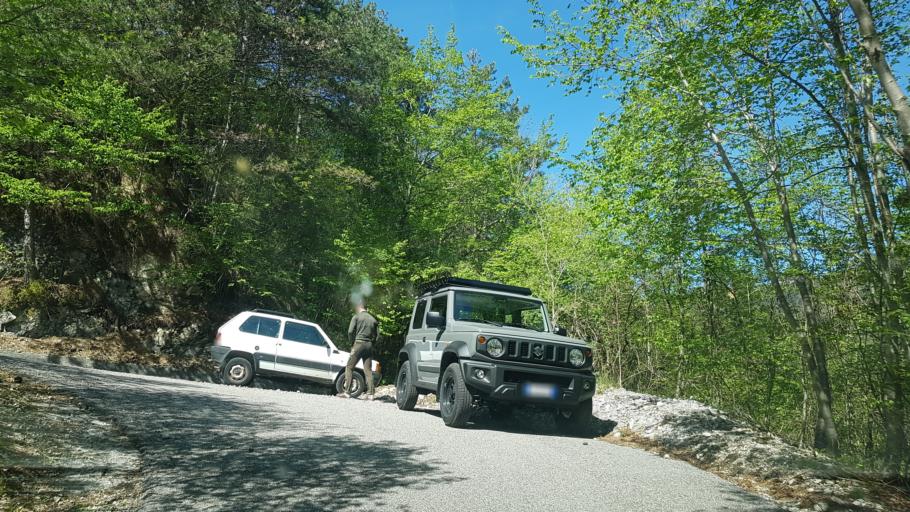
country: IT
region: Friuli Venezia Giulia
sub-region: Provincia di Udine
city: Trasaghis
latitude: 46.3154
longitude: 13.0386
